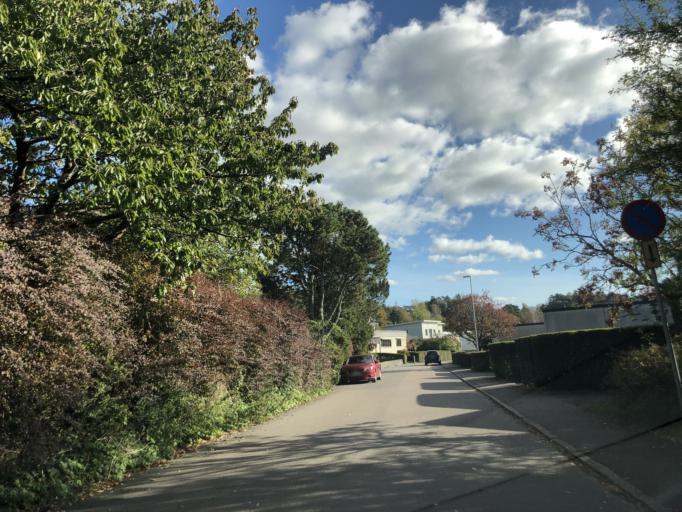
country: SE
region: Vaestra Goetaland
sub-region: Goteborg
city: Majorna
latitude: 57.6333
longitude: 11.9380
